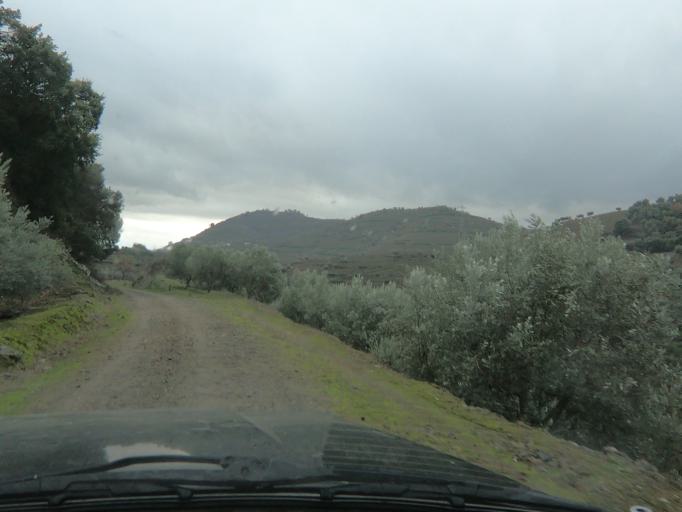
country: PT
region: Vila Real
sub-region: Santa Marta de Penaguiao
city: Santa Marta de Penaguiao
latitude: 41.2032
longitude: -7.7608
